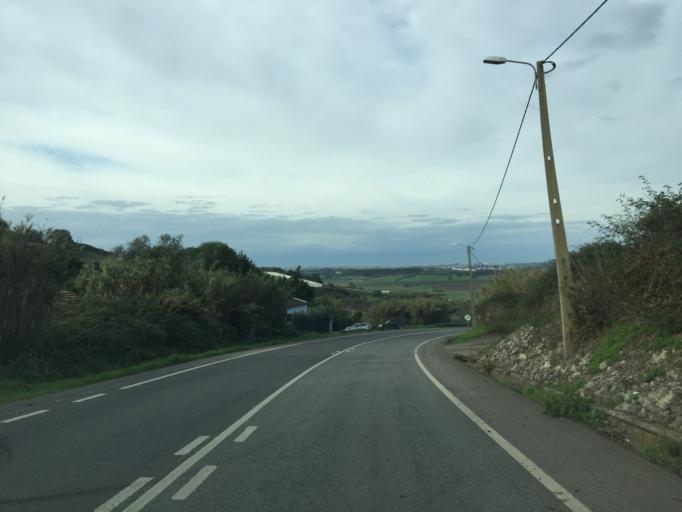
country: PT
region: Lisbon
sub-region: Sintra
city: Almargem
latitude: 38.8511
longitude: -9.2667
